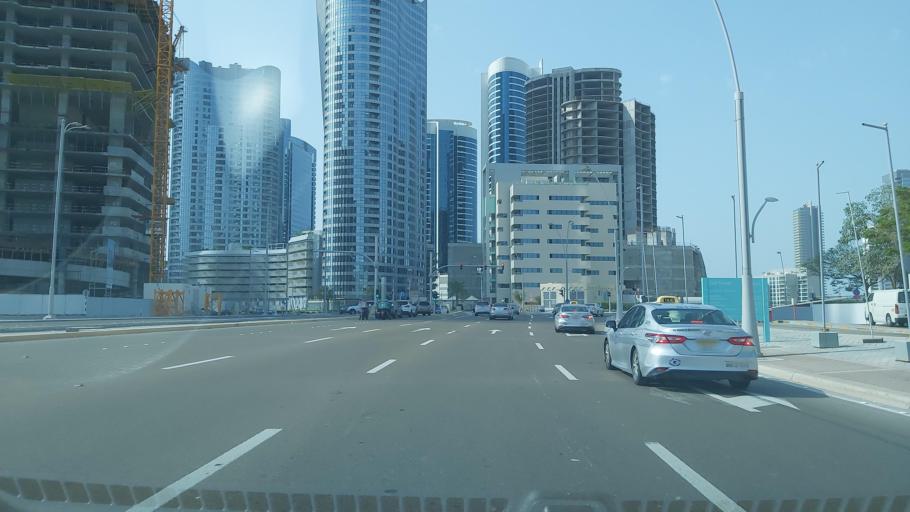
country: AE
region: Abu Dhabi
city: Abu Dhabi
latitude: 24.4958
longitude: 54.4058
